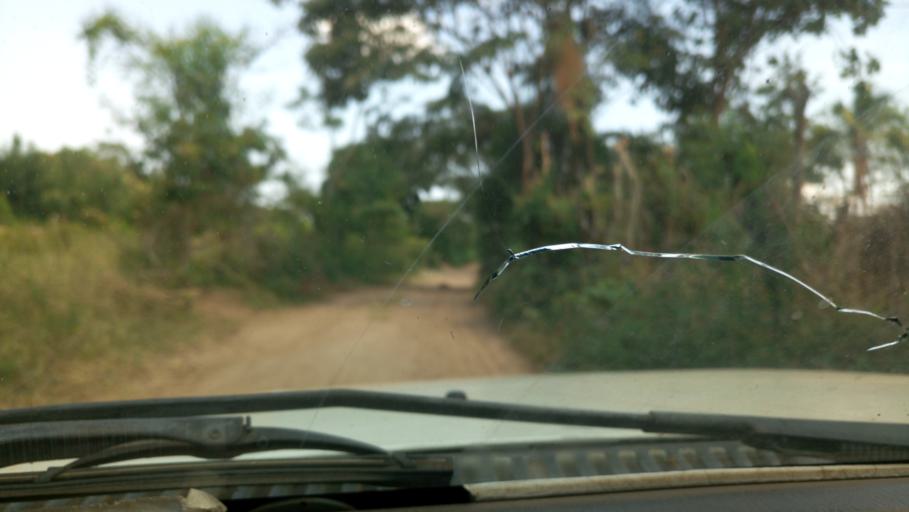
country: KE
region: Murang'a District
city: Karuri
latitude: -0.6946
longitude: 37.1885
